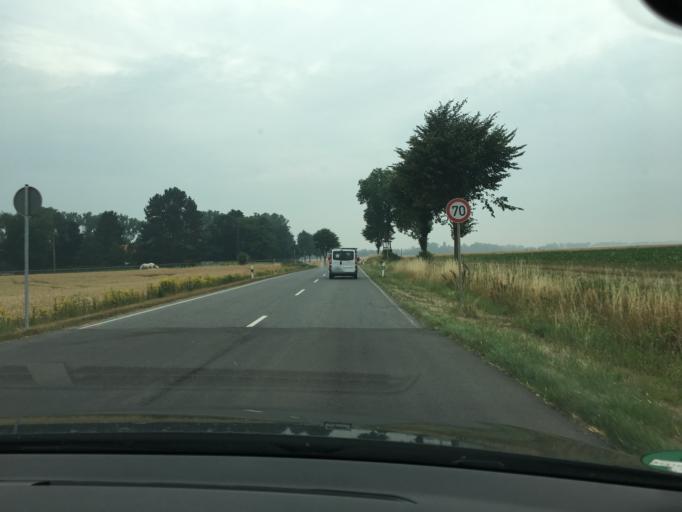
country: DE
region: North Rhine-Westphalia
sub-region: Regierungsbezirk Koln
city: Titz
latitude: 51.0288
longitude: 6.3895
